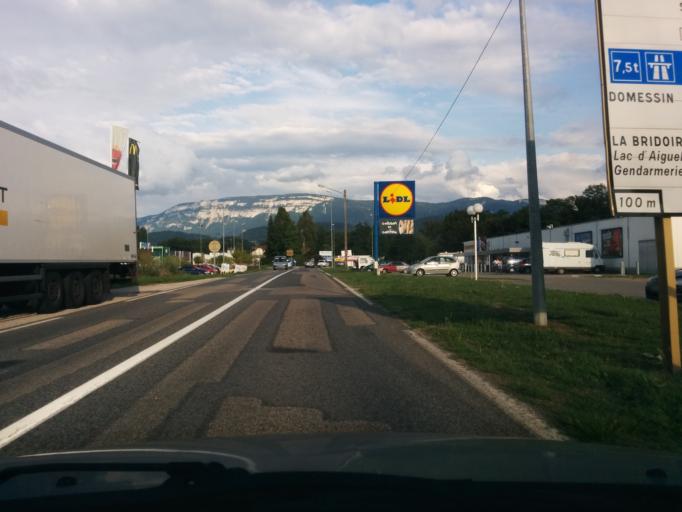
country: FR
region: Rhone-Alpes
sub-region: Departement de la Savoie
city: Domessin
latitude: 45.5290
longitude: 5.6874
